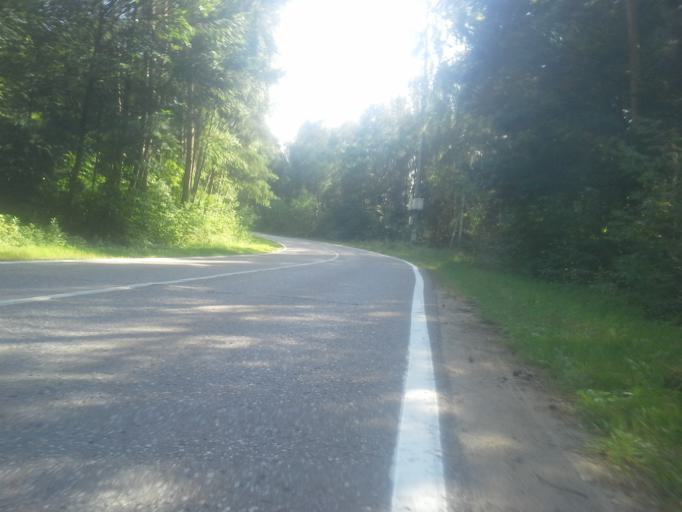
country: RU
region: Moskovskaya
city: Karinskoye
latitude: 55.7007
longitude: 36.6988
